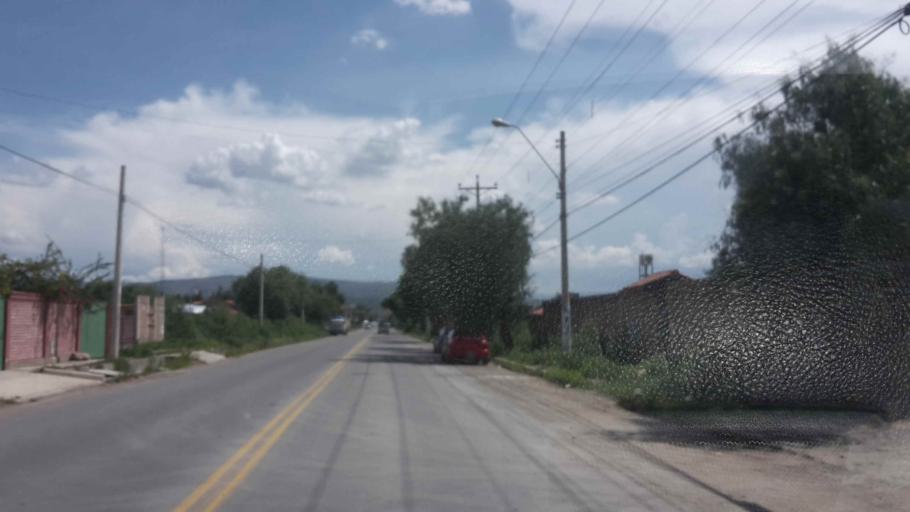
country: BO
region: Cochabamba
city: Cochabamba
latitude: -17.3792
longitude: -66.2350
